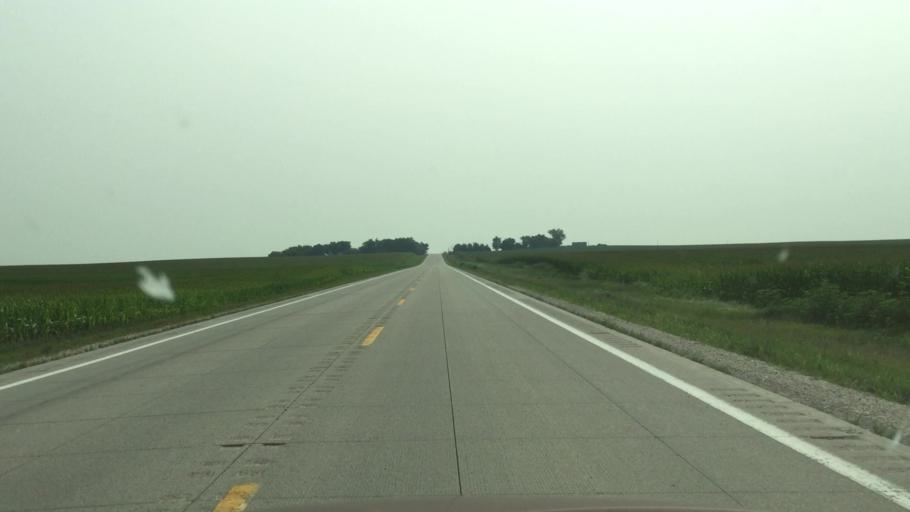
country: US
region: Iowa
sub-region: Osceola County
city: Sibley
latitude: 43.4327
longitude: -95.6731
